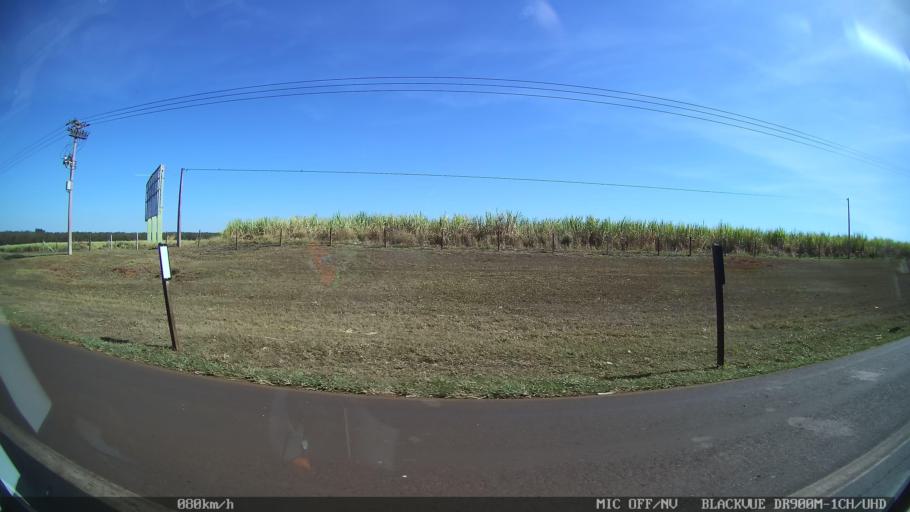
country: BR
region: Sao Paulo
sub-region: Barretos
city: Barretos
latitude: -20.5803
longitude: -48.5812
